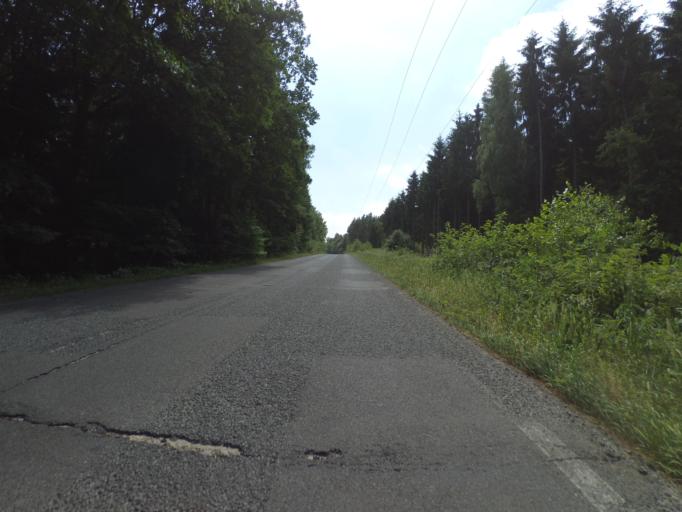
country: DE
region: Mecklenburg-Vorpommern
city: Plau am See
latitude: 53.4022
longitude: 12.3223
